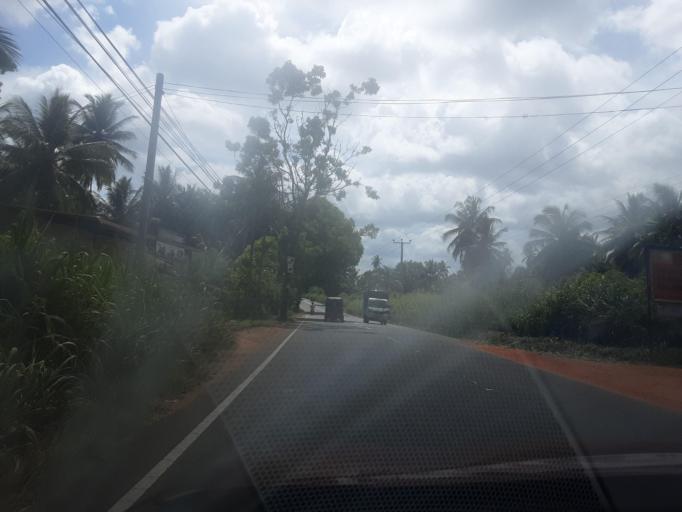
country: LK
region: North Western
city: Kuliyapitiya
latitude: 7.4816
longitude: 79.9878
